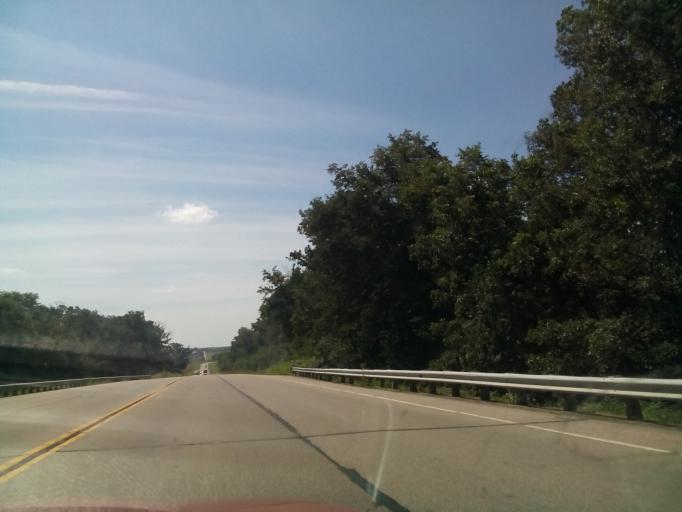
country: US
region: Wisconsin
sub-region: Green County
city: Monticello
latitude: 42.7313
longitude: -89.5988
